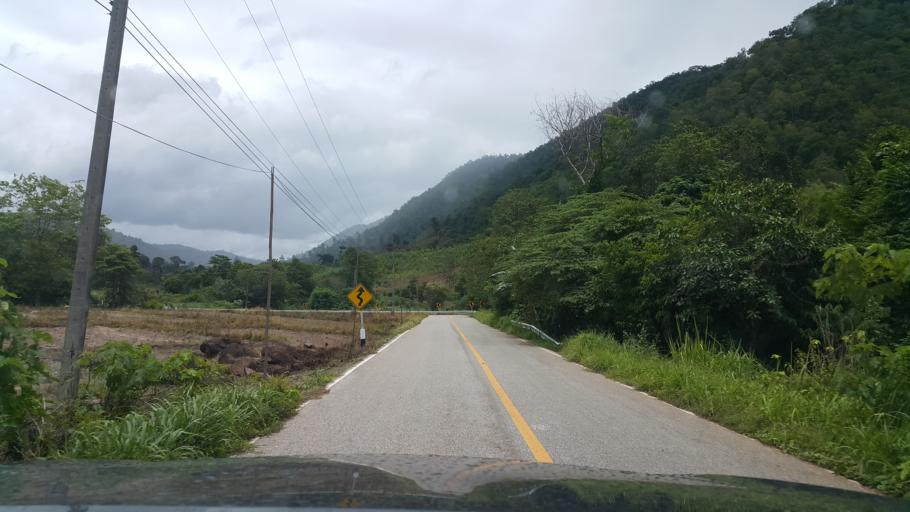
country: TH
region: Loei
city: Na Haeo
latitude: 17.5496
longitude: 100.8420
